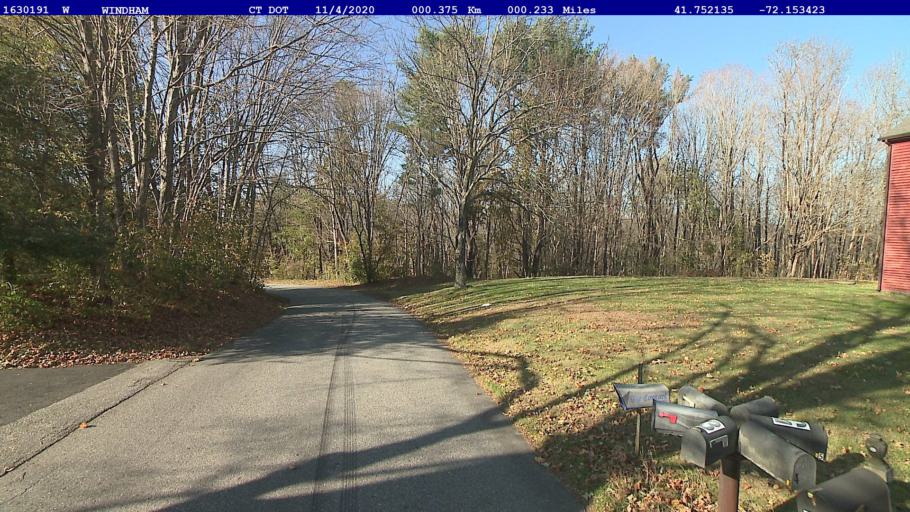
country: US
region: Connecticut
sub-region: Windham County
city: Windham
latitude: 41.7521
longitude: -72.1534
